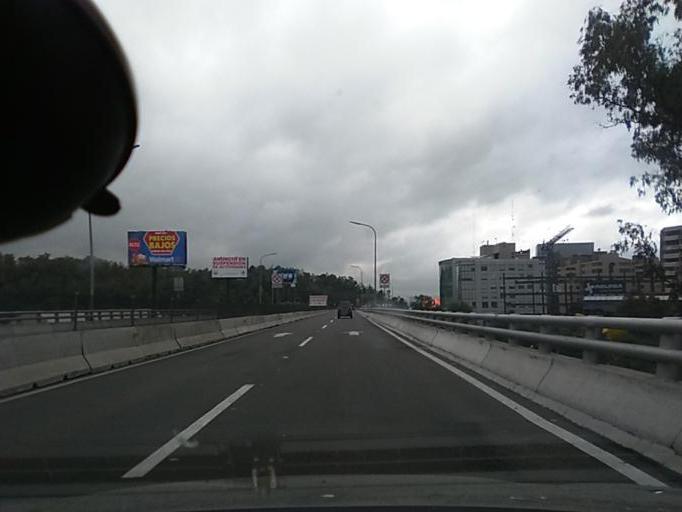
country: MX
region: Mexico City
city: Magdalena Contreras
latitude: 19.3056
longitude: -99.2055
